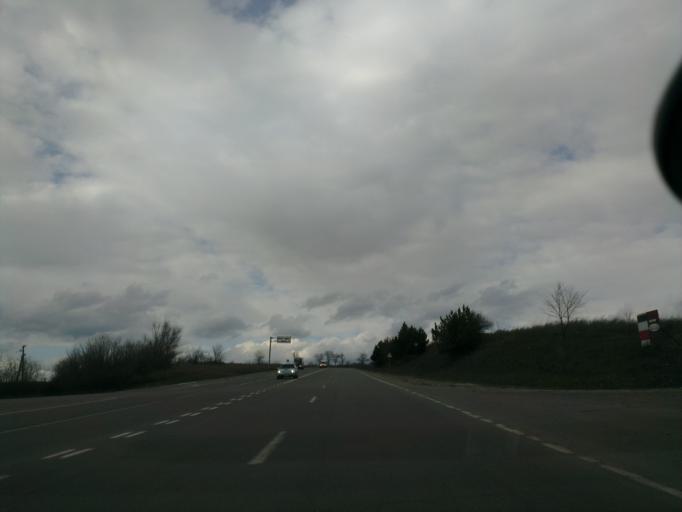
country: MD
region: Laloveni
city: Ialoveni
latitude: 46.9183
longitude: 28.6917
